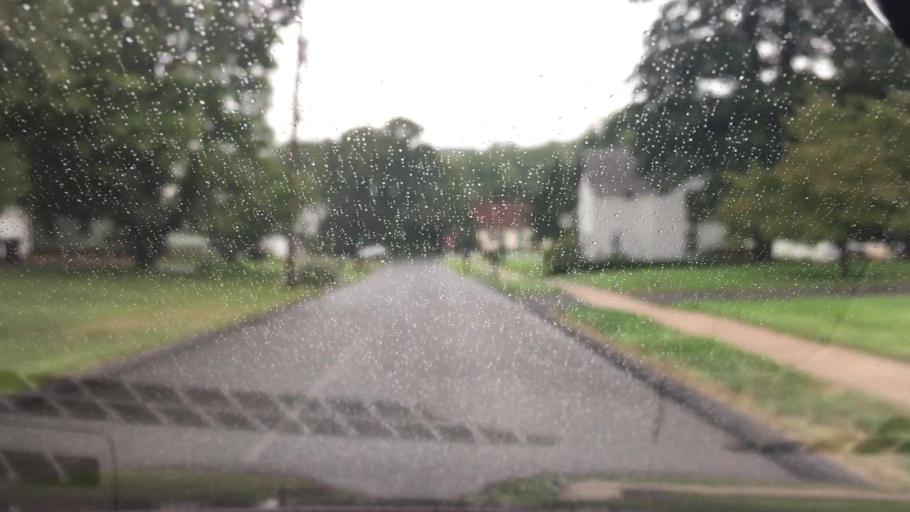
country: US
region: Connecticut
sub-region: Hartford County
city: Kensington
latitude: 41.6151
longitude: -72.7154
